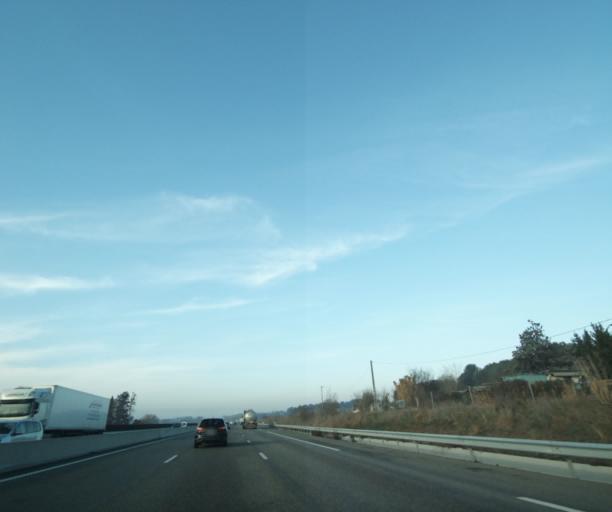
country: FR
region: Provence-Alpes-Cote d'Azur
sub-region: Departement des Bouches-du-Rhone
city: Trets
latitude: 43.4707
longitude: 5.6770
